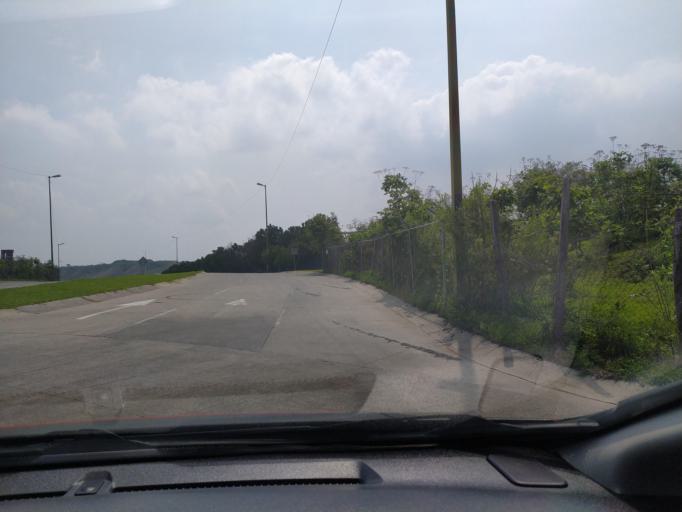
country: MX
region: Jalisco
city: Guadalajara
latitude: 20.6694
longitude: -103.4655
